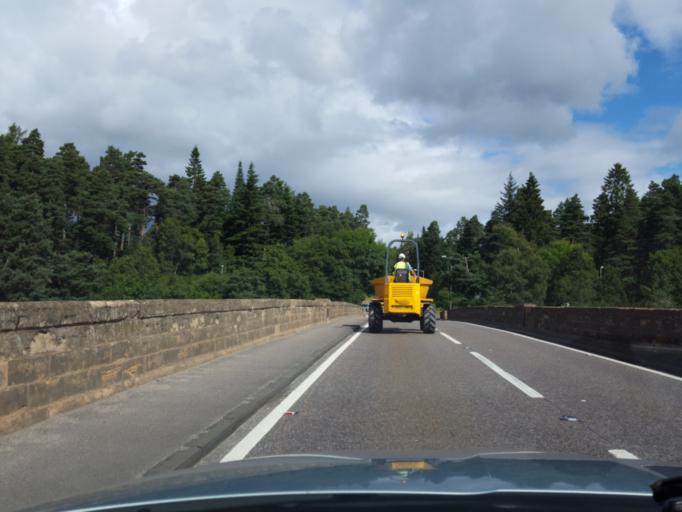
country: GB
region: Scotland
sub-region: Highland
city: Grantown on Spey
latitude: 57.3211
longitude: -3.6060
